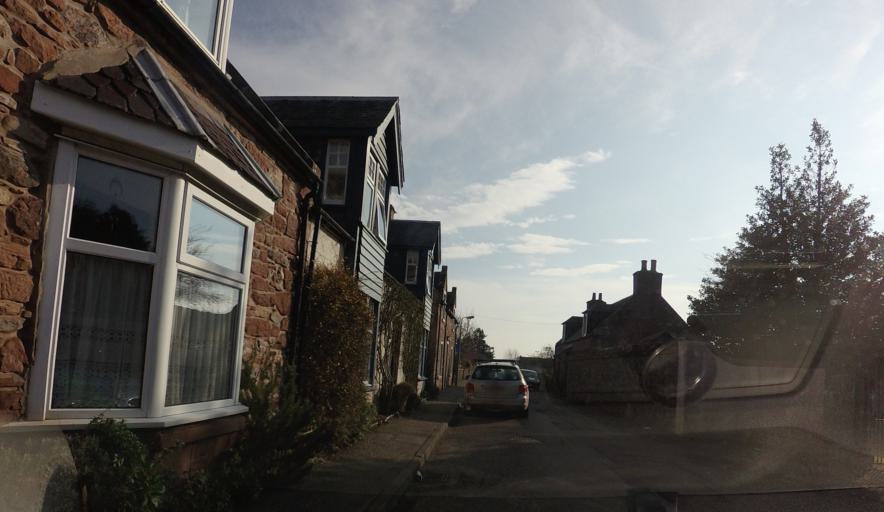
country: GB
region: Scotland
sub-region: Highland
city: Fortrose
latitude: 57.5817
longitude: -4.1293
